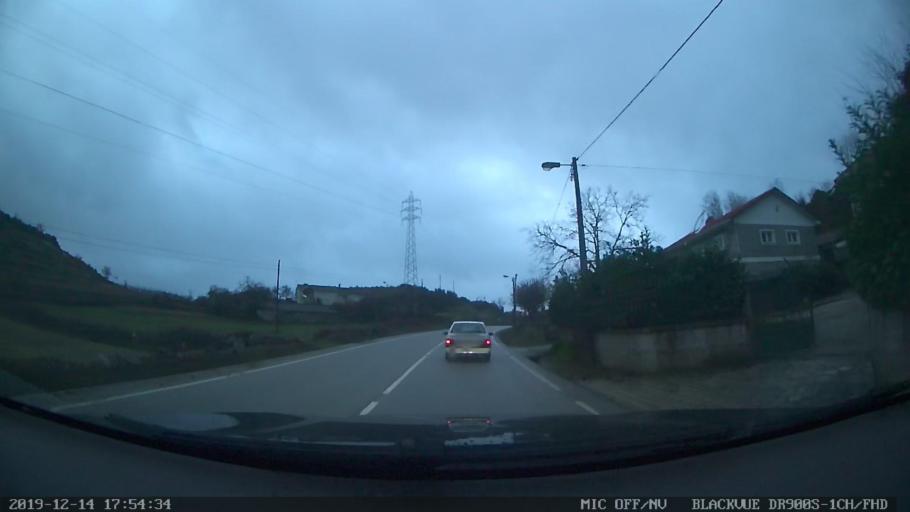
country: PT
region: Vila Real
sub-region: Vila Pouca de Aguiar
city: Vila Pouca de Aguiar
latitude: 41.4117
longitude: -7.6878
